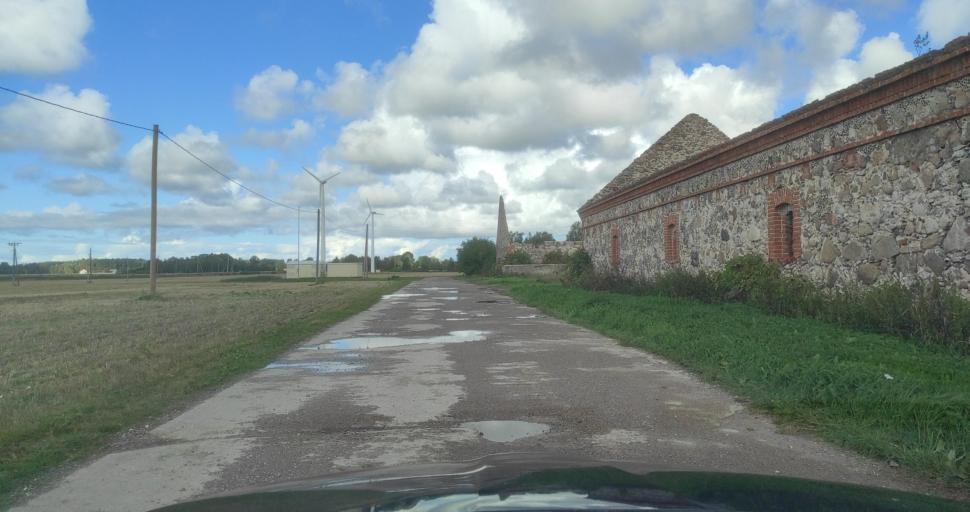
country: LV
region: Ventspils Rajons
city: Piltene
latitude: 57.2654
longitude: 21.5892
